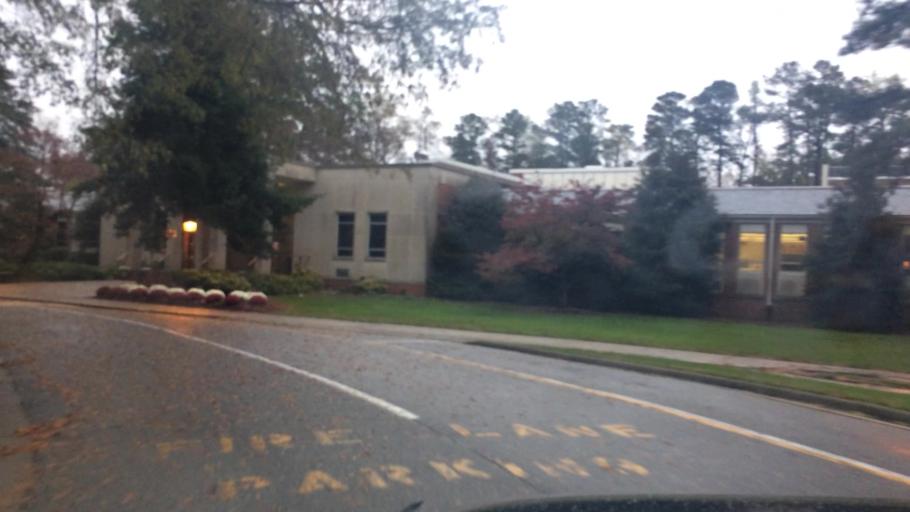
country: US
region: Virginia
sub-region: James City County
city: Williamsburg
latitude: 37.2565
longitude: -76.7265
